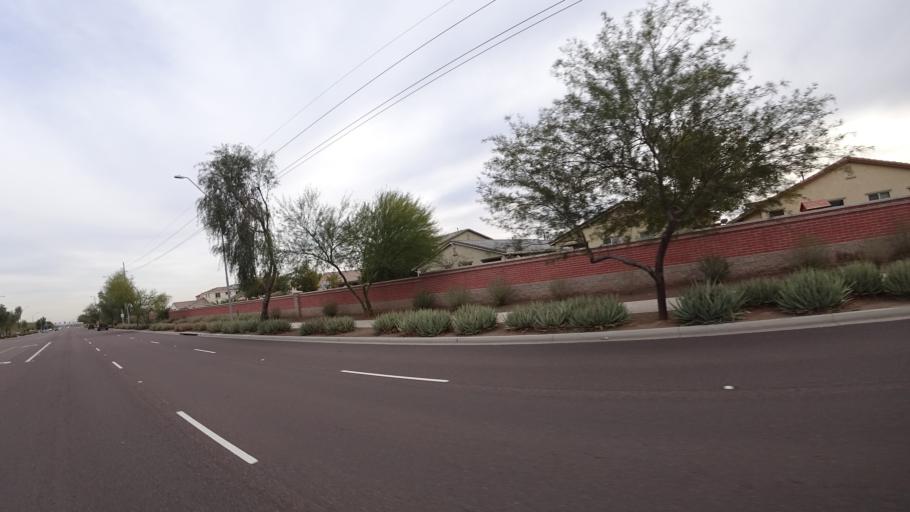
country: US
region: Arizona
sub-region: Maricopa County
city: Surprise
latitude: 33.6093
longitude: -112.3818
